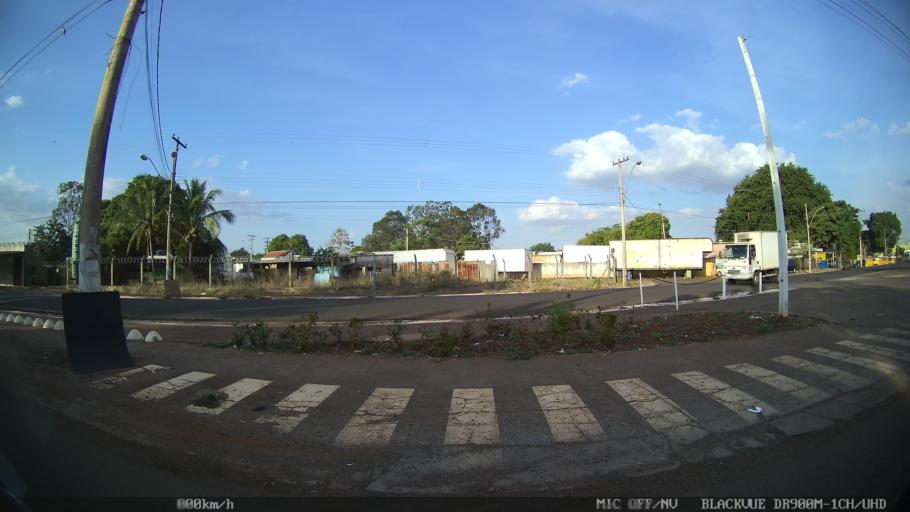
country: BR
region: Sao Paulo
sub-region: Ribeirao Preto
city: Ribeirao Preto
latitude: -21.1257
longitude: -47.7853
